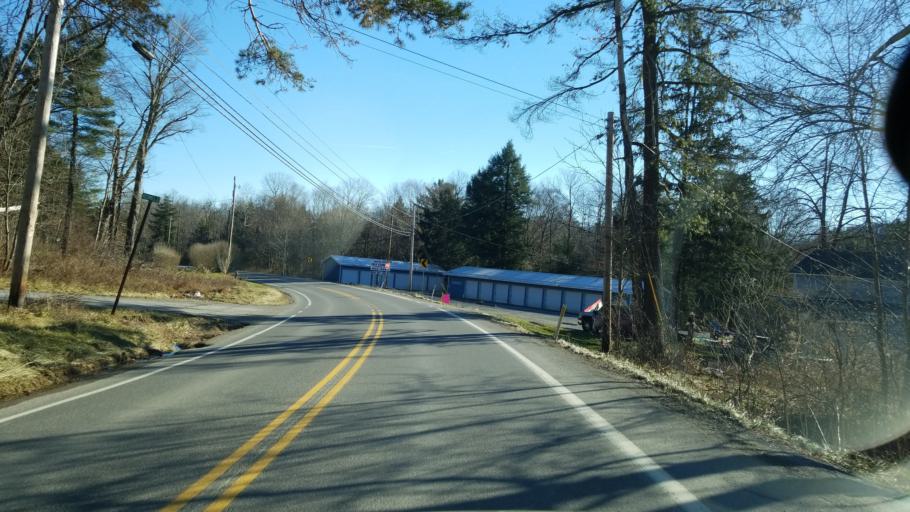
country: US
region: Pennsylvania
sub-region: Jefferson County
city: Falls Creek
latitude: 41.1556
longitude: -78.8226
